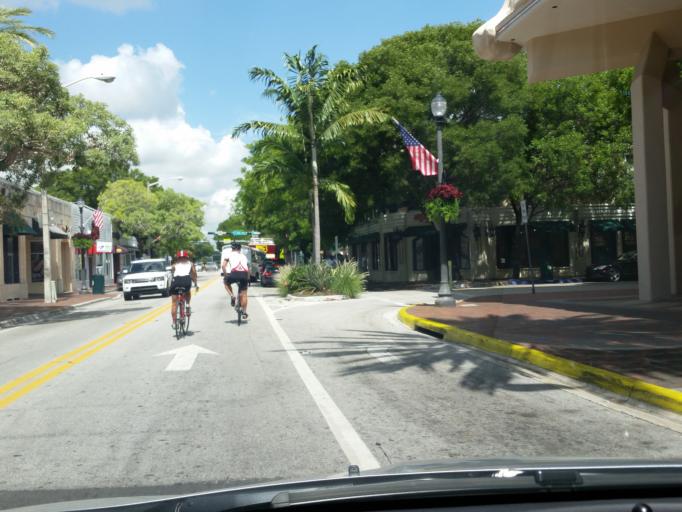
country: US
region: Florida
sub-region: Miami-Dade County
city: Coconut Grove
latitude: 25.7281
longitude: -80.2412
